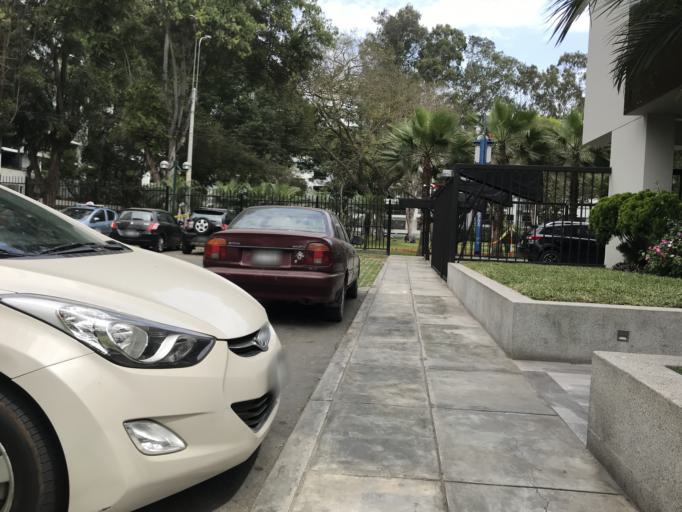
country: PE
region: Lima
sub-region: Lima
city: San Isidro
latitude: -12.1115
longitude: -77.0436
